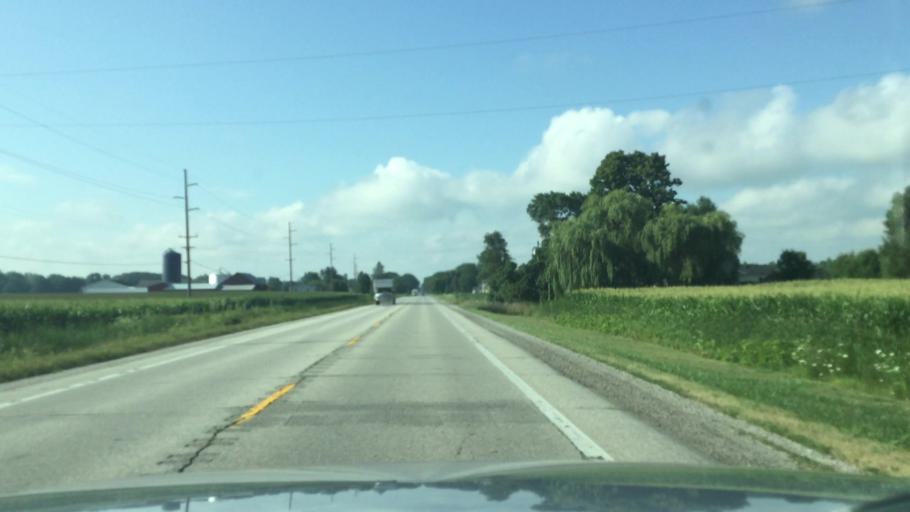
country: US
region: Michigan
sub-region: Saginaw County
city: Frankenmuth
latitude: 43.2763
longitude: -83.7358
